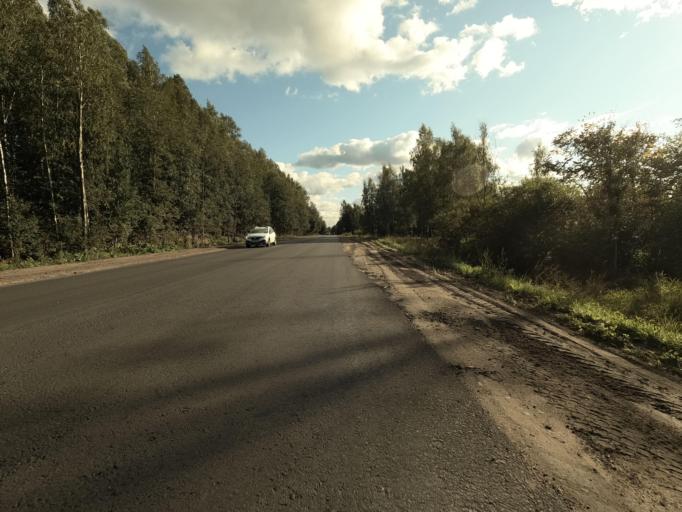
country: RU
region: Leningrad
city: Koltushi
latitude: 59.9299
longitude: 30.6643
